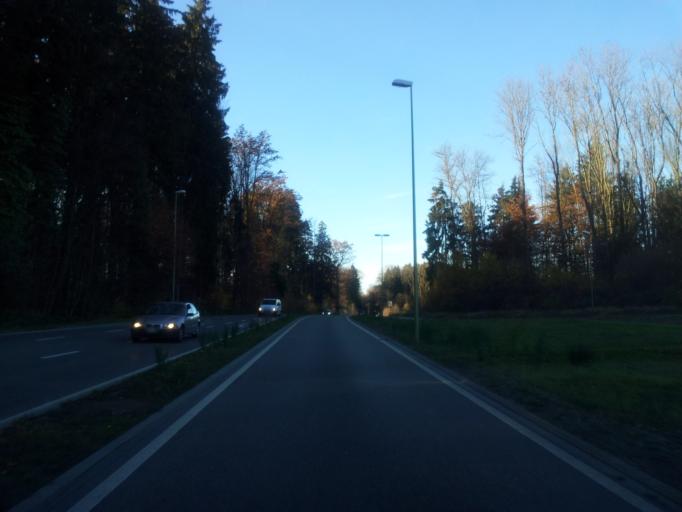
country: CH
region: Zurich
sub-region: Bezirk Buelach
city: Glattbrugg
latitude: 47.4365
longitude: 8.5538
